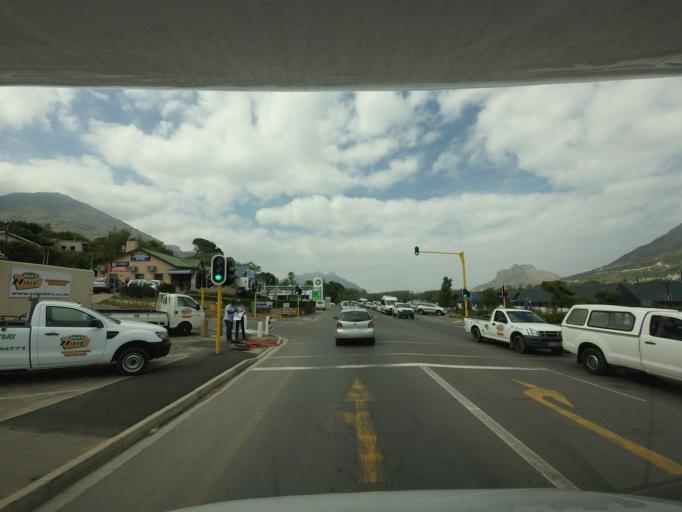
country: ZA
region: Western Cape
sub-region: City of Cape Town
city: Constantia
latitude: -34.0333
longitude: 18.3564
